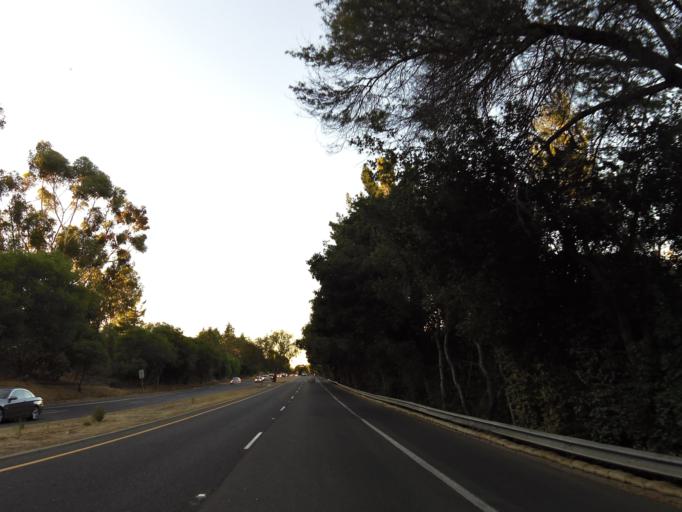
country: US
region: California
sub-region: Santa Clara County
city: Los Altos Hills
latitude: 37.3914
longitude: -122.1287
